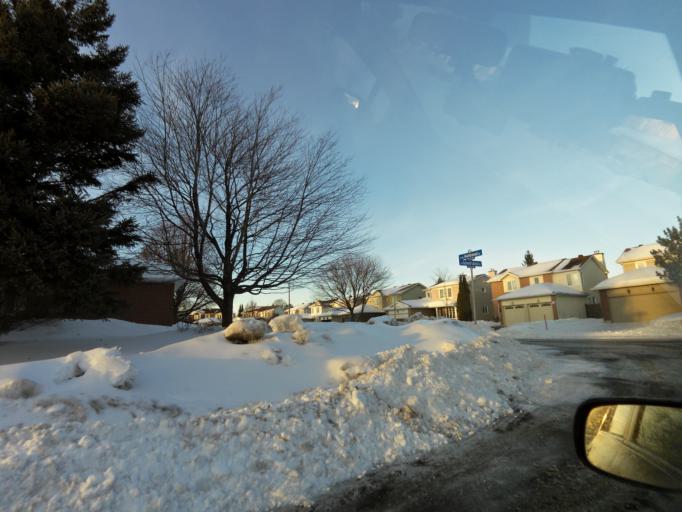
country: CA
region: Ontario
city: Ottawa
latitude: 45.4433
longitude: -75.5270
